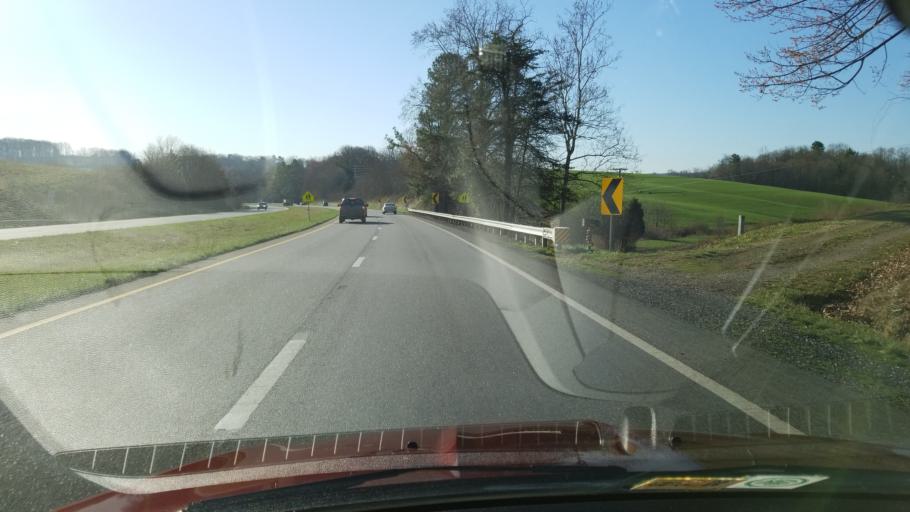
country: US
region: Virginia
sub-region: Franklin County
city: Rocky Mount
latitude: 37.0926
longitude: -79.9381
